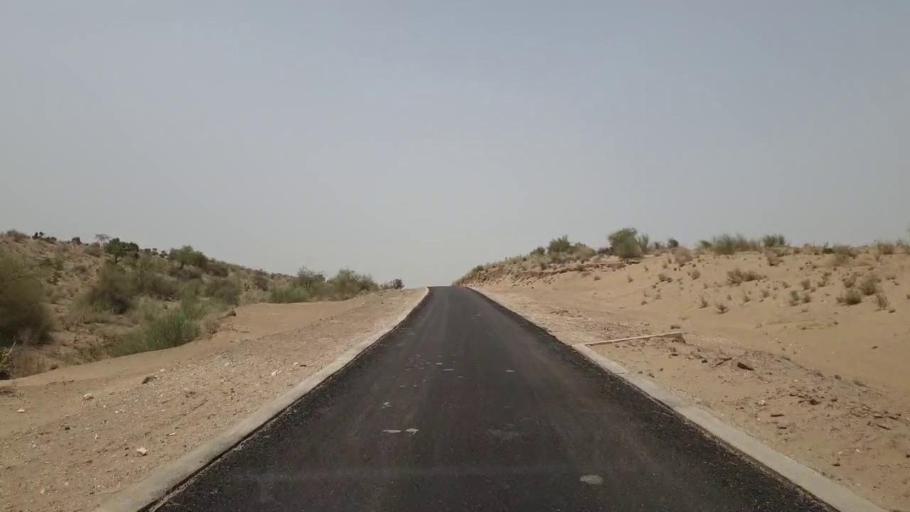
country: PK
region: Sindh
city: Islamkot
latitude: 24.8001
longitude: 70.5505
